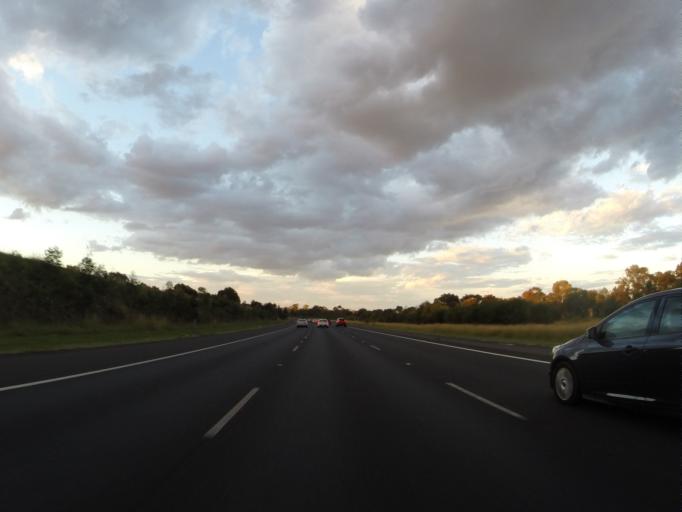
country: AU
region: New South Wales
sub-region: Campbelltown Municipality
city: Leumeah
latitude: -34.0425
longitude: 150.8211
